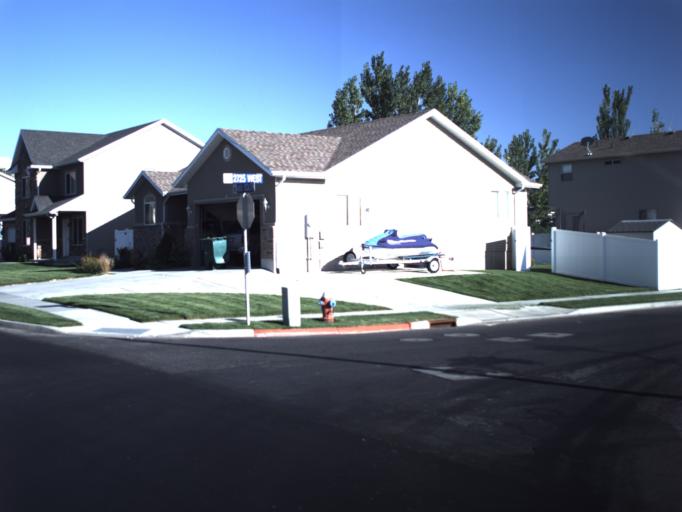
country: US
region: Utah
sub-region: Weber County
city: West Haven
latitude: 41.1906
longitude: -112.0460
